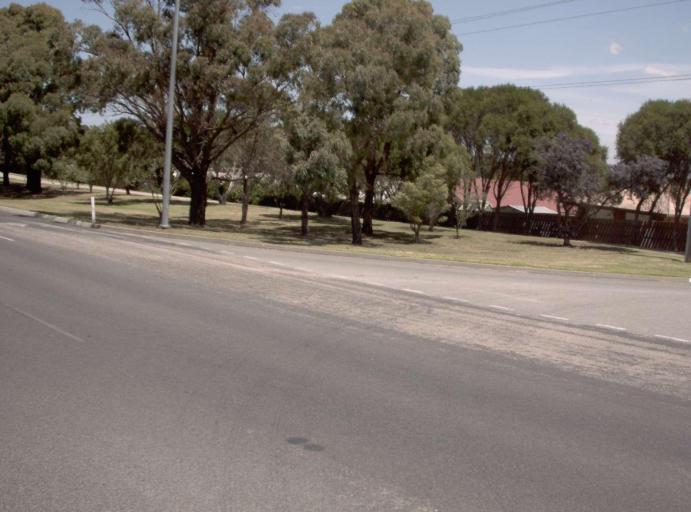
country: AU
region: Victoria
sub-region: East Gippsland
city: Bairnsdale
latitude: -37.8162
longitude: 147.6485
